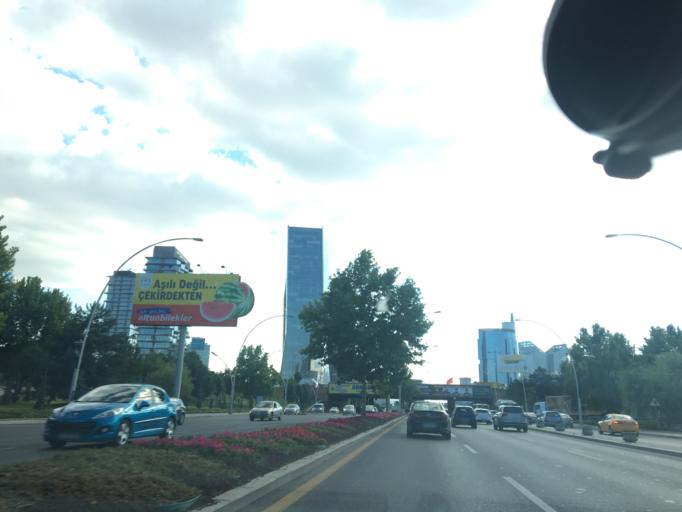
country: TR
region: Ankara
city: Ankara
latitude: 39.9133
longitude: 32.8167
